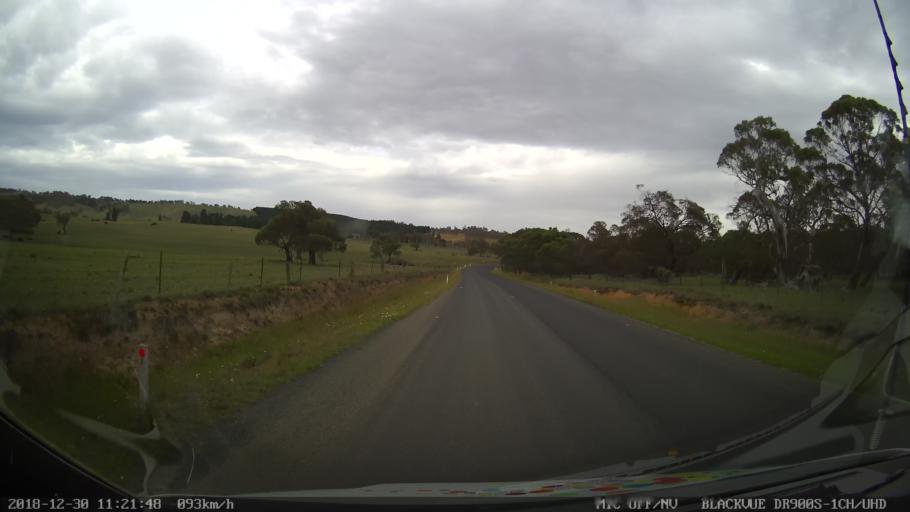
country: AU
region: New South Wales
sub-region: Snowy River
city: Jindabyne
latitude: -36.5068
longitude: 148.6735
